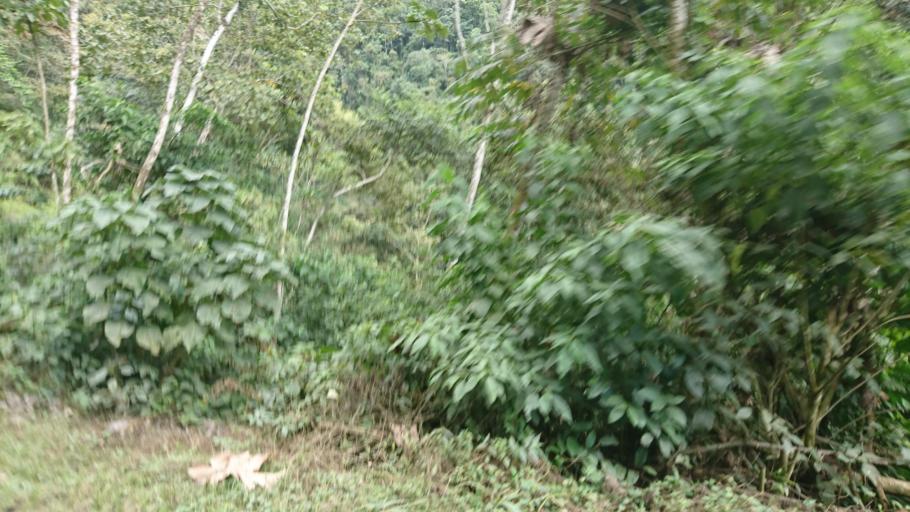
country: BO
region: La Paz
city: Coroico
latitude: -16.1147
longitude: -67.7832
